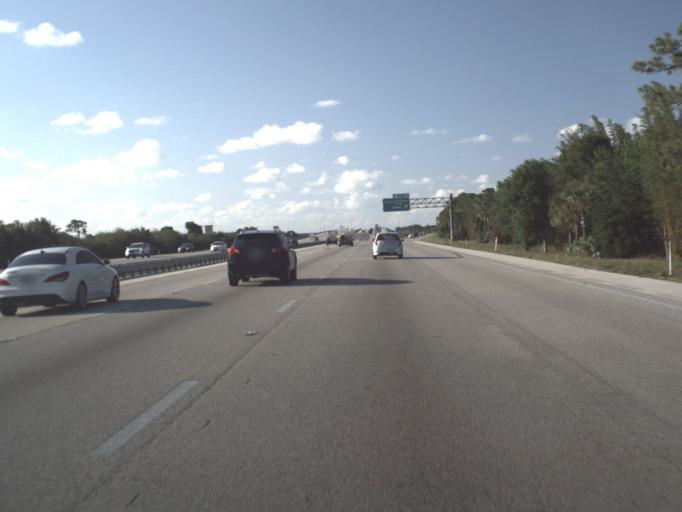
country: US
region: Florida
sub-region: Brevard County
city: South Patrick Shores
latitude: 28.2223
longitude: -80.7160
